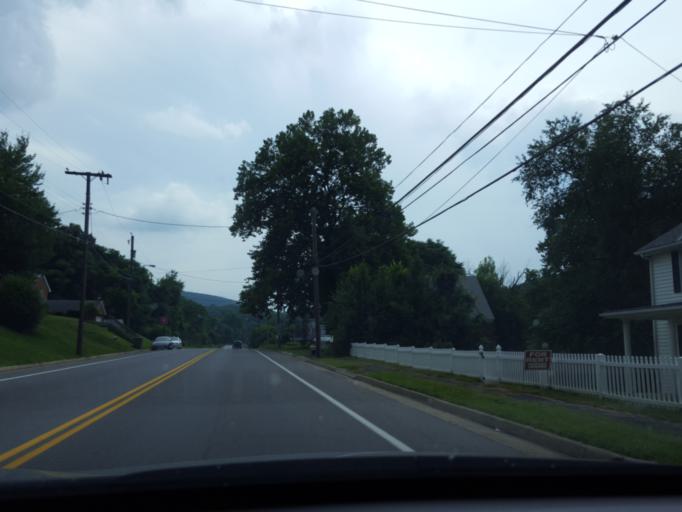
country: US
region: Virginia
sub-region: City of Waynesboro
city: Waynesboro
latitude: 38.0627
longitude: -78.8721
